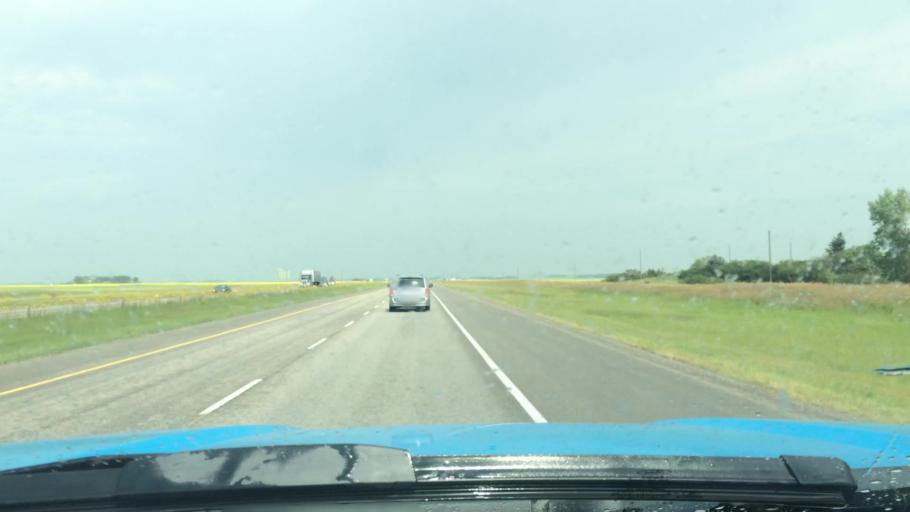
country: CA
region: Alberta
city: Didsbury
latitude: 51.6727
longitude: -114.0253
